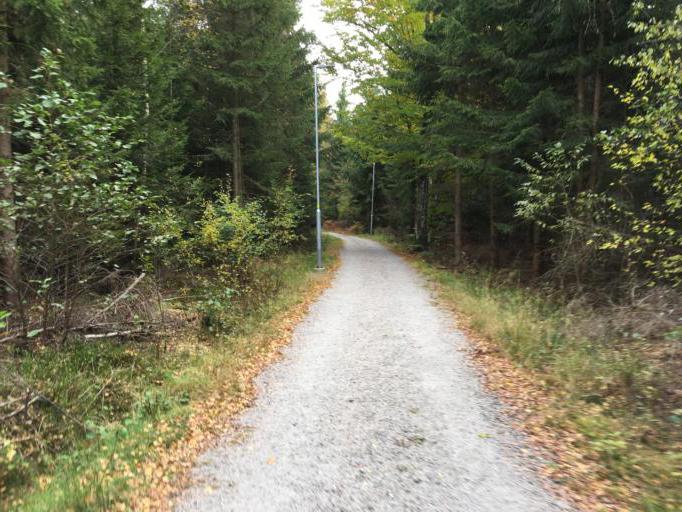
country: SE
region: Skane
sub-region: Hassleholms Kommun
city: Hassleholm
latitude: 56.1562
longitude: 13.7265
